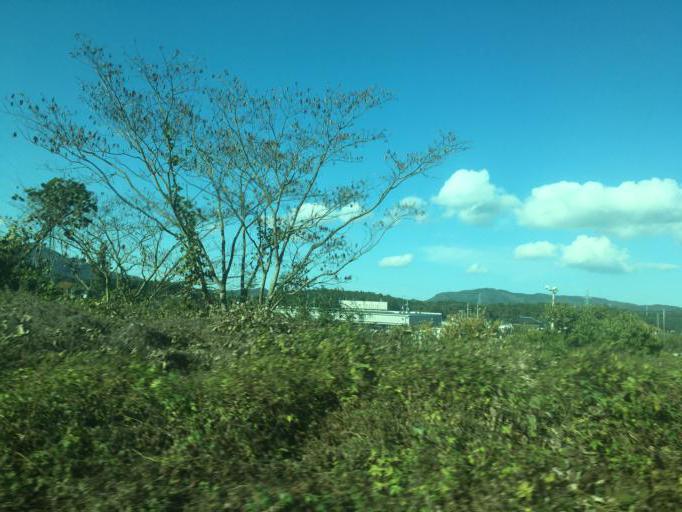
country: JP
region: Ibaraki
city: Kasama
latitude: 36.3767
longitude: 140.2301
